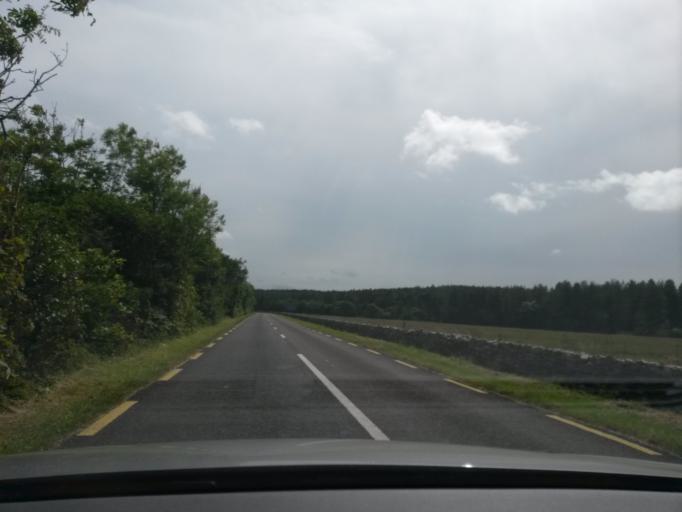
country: IE
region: Connaught
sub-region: County Leitrim
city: Kinlough
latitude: 54.4513
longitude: -8.4526
